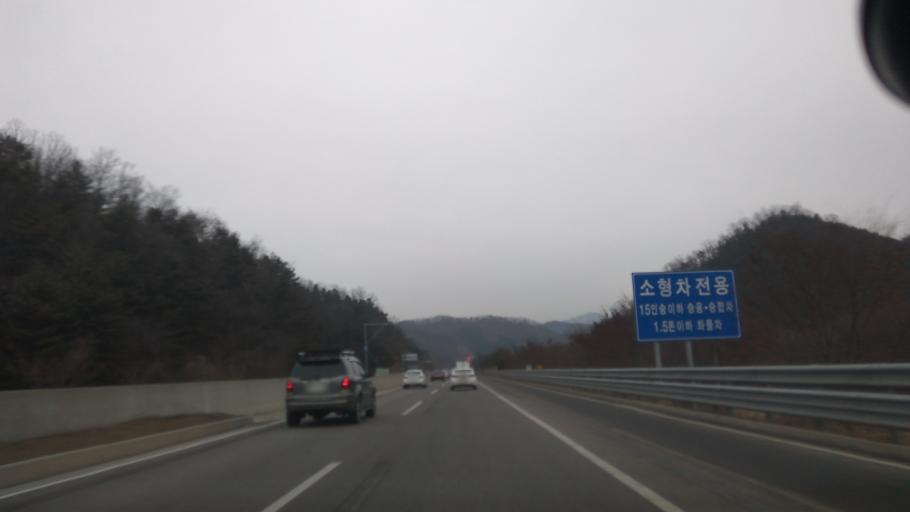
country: KR
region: Gangwon-do
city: Sindong
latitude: 37.7408
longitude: 127.6673
